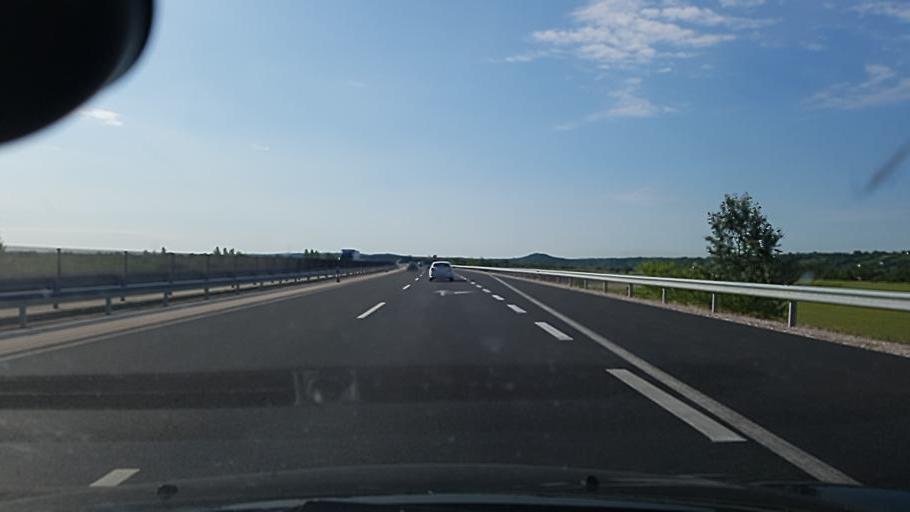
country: HU
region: Fejer
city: Adony
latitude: 47.0956
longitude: 18.8504
